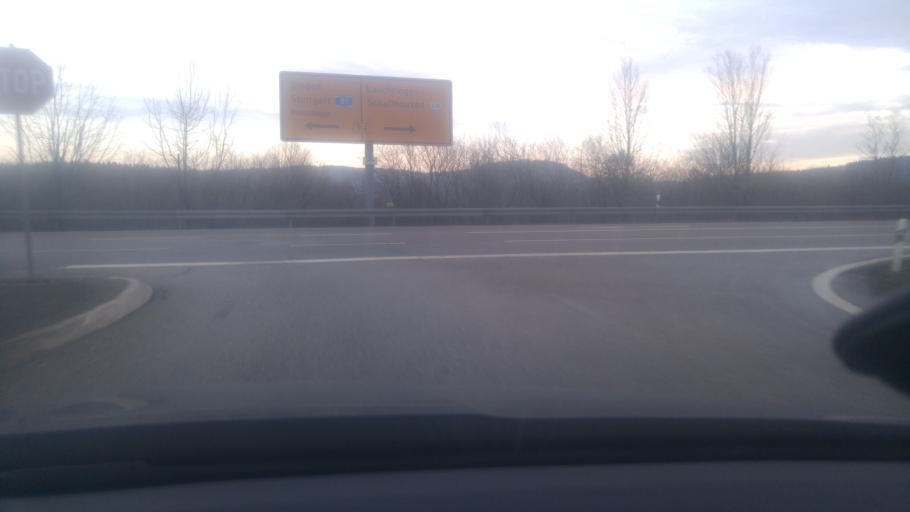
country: DE
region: Baden-Wuerttemberg
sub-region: Freiburg Region
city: Lauchringen
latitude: 47.6302
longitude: 8.3327
